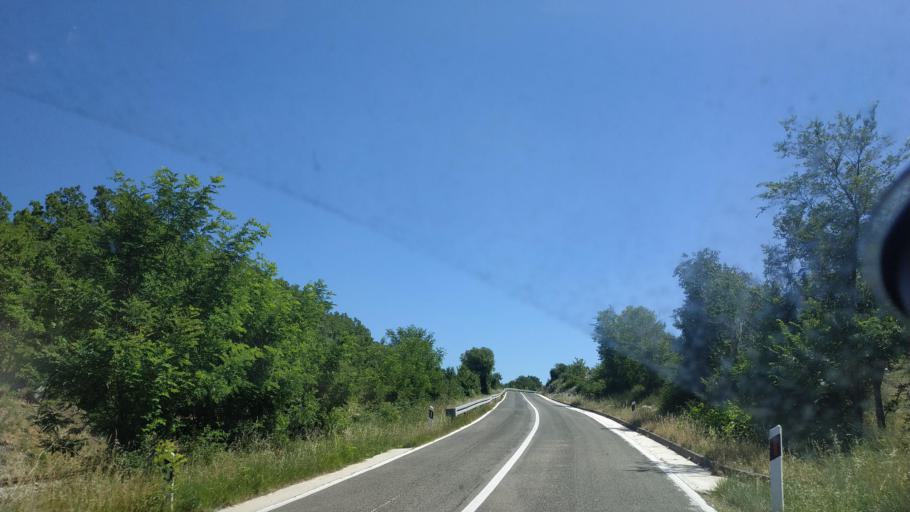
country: HR
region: Sibensko-Kniniska
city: Drnis
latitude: 43.9007
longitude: 16.2096
